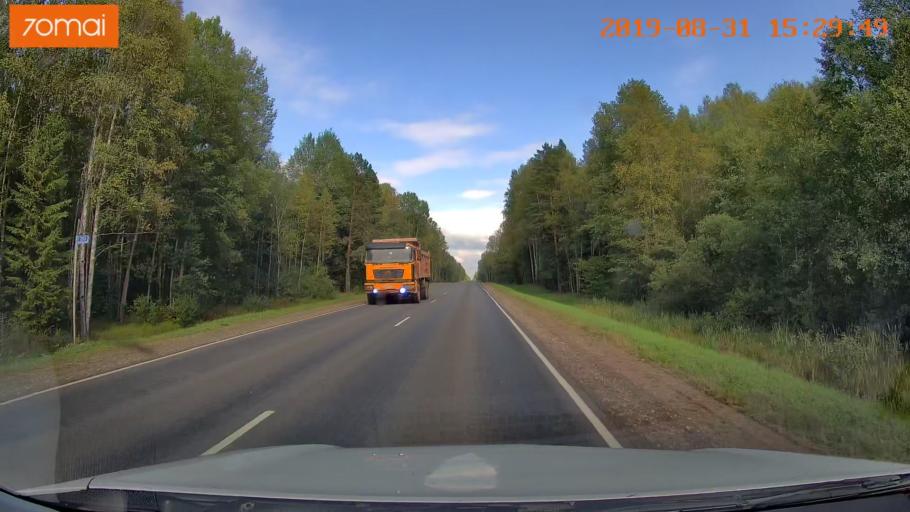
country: RU
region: Kaluga
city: Baryatino
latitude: 54.5715
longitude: 34.6148
